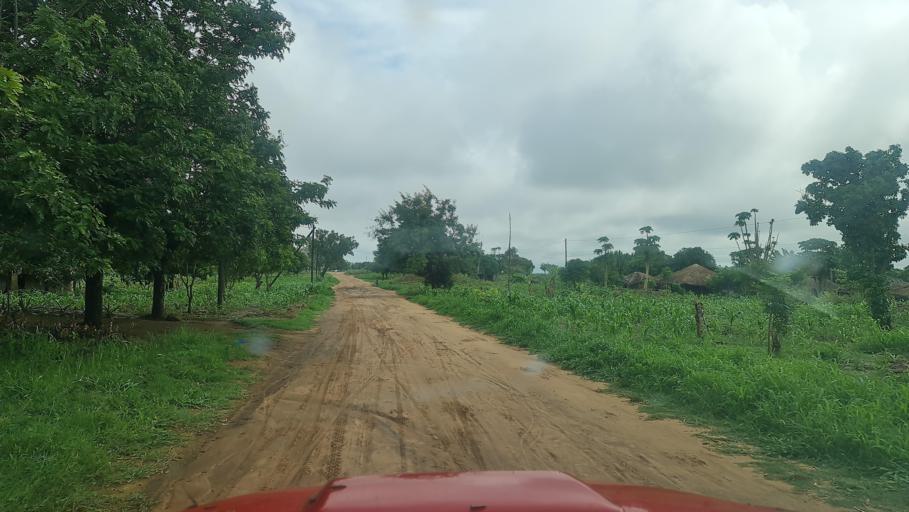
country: MW
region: Southern Region
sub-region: Nsanje District
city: Nsanje
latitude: -17.2193
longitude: 35.6738
